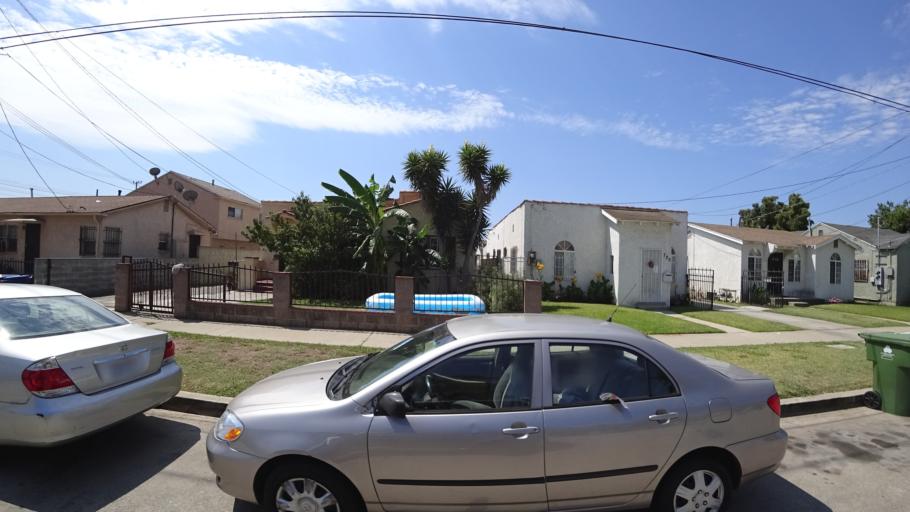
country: US
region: California
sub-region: Los Angeles County
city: Westmont
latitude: 33.9501
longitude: -118.2878
